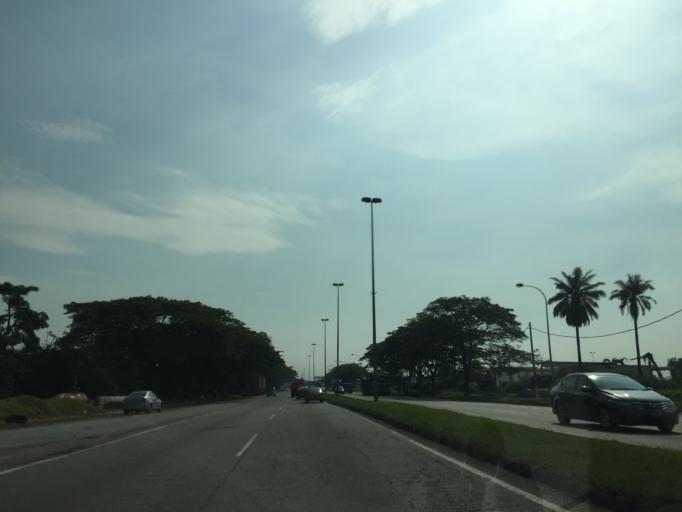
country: MY
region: Selangor
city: Klang
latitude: 2.9837
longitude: 101.4398
